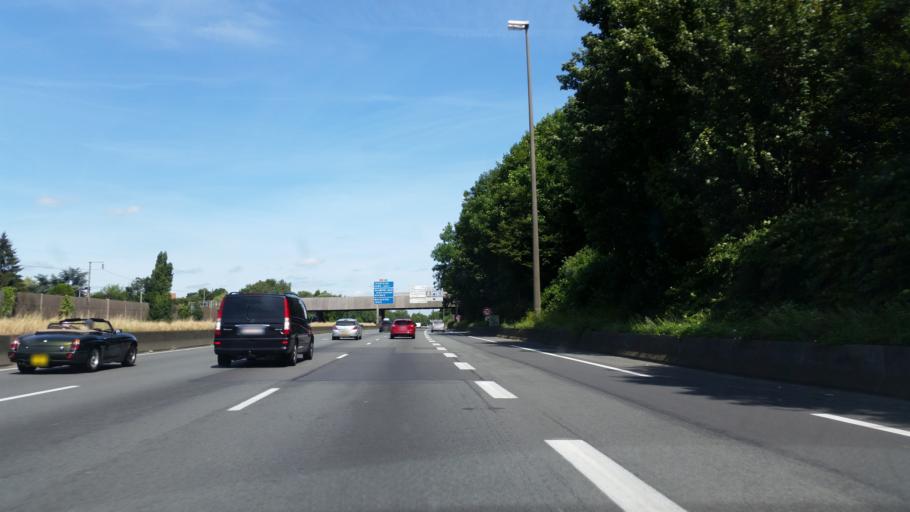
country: FR
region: Nord-Pas-de-Calais
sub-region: Departement du Nord
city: La Madeleine
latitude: 50.6457
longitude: 3.0961
